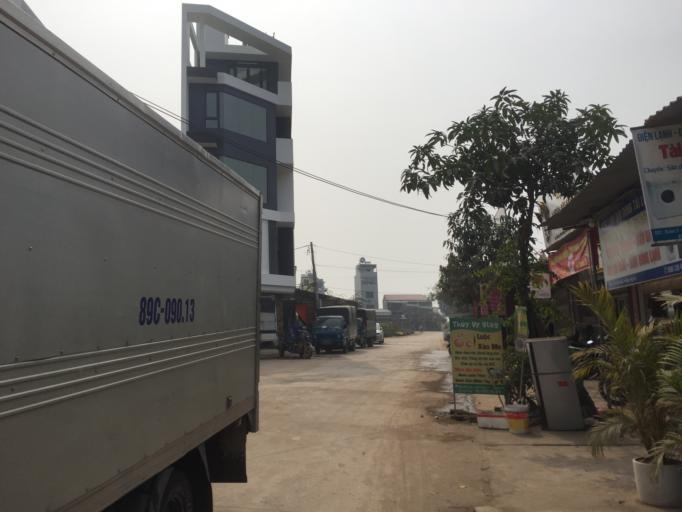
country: VN
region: Hung Yen
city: Van Giang
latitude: 20.9625
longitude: 105.9176
